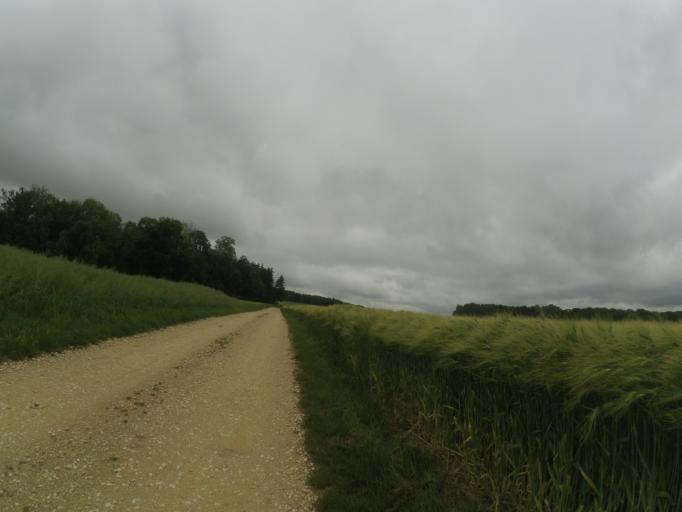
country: DE
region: Baden-Wuerttemberg
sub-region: Tuebingen Region
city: Bernstadt
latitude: 48.4587
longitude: 10.0506
